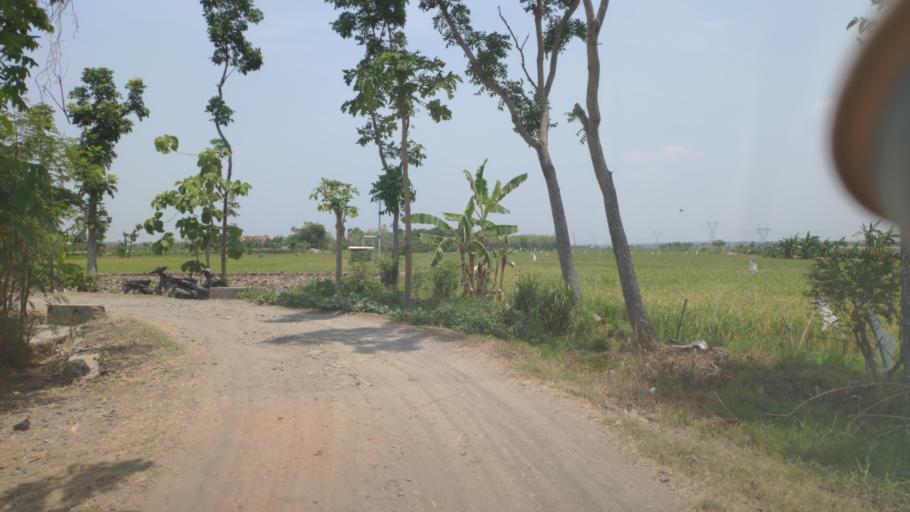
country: ID
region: Central Java
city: Temulus
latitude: -7.2272
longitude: 111.4297
